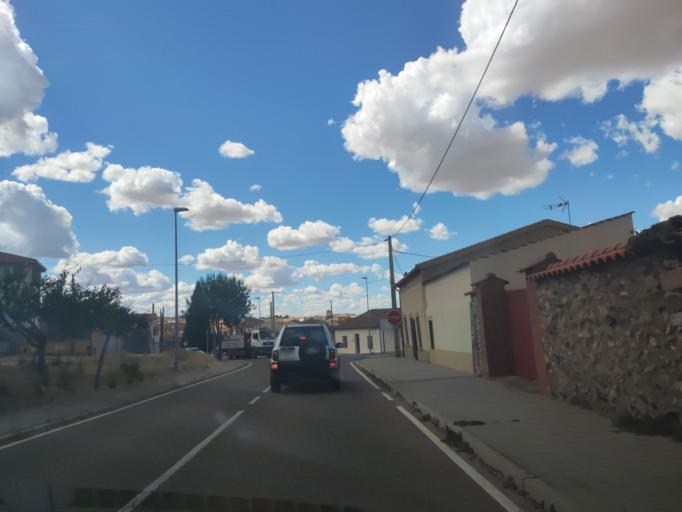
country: ES
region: Castille and Leon
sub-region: Provincia de Salamanca
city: Tamames
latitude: 40.6549
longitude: -6.0998
